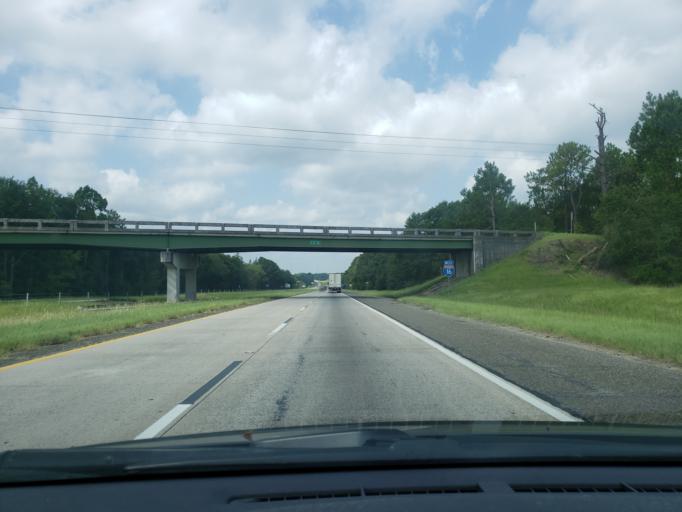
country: US
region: Georgia
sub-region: Treutlen County
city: Soperton
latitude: 32.4342
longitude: -82.5095
